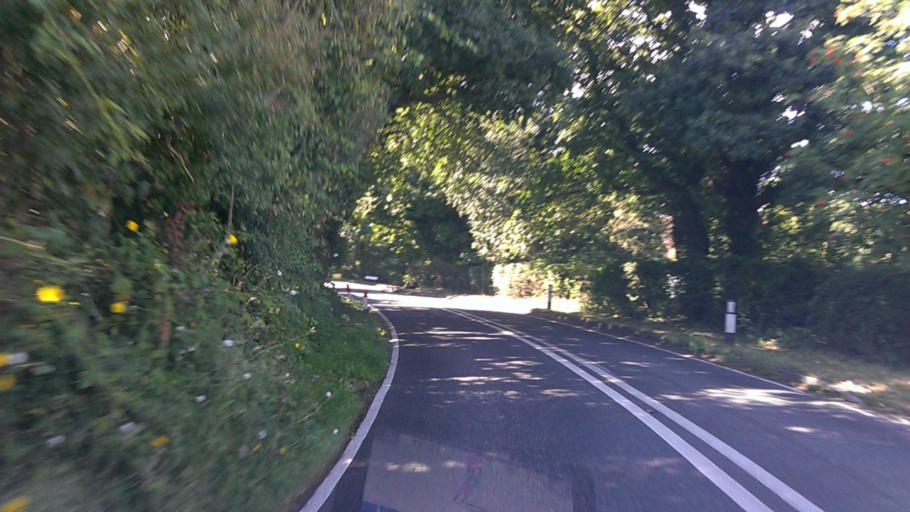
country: GB
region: England
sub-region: Essex
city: Layer de la Haye
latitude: 51.8461
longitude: 0.8795
